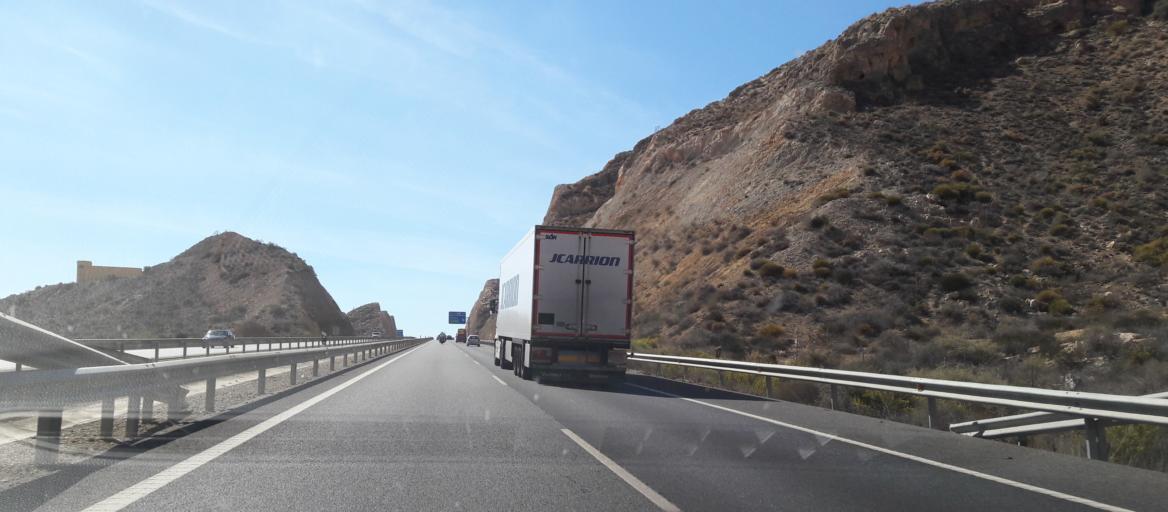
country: ES
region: Andalusia
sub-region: Provincia de Almeria
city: Huercal de Almeria
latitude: 36.8855
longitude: -2.4562
